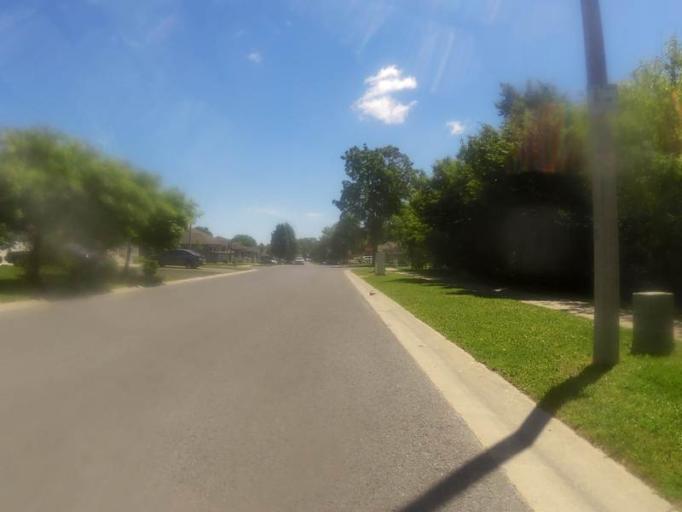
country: CA
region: Ontario
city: Kingston
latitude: 44.2601
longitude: -76.5498
